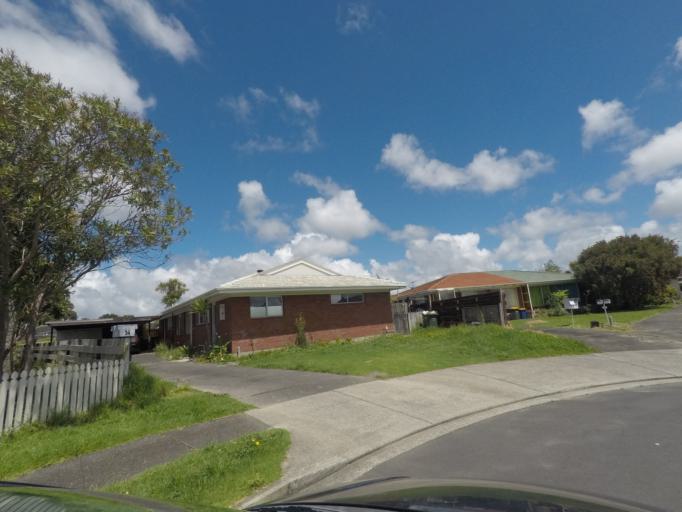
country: NZ
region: Auckland
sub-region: Auckland
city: Rosebank
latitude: -36.8796
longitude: 174.6429
